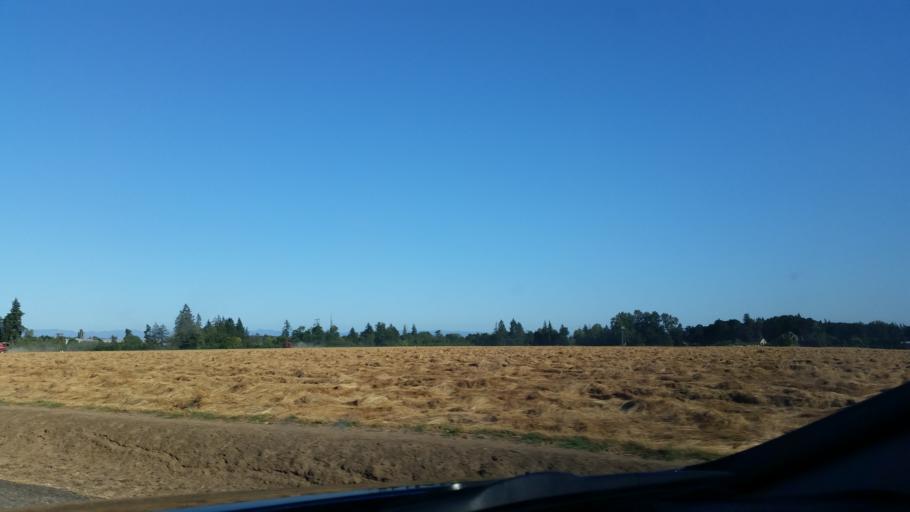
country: US
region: Oregon
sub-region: Marion County
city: Hubbard
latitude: 45.2279
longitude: -122.8636
